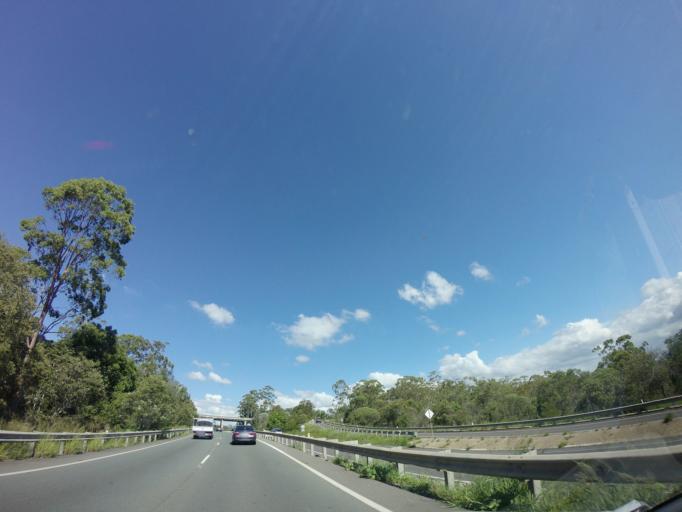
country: AU
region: Queensland
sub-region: Ipswich
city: Brassall
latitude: -27.5805
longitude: 152.7515
